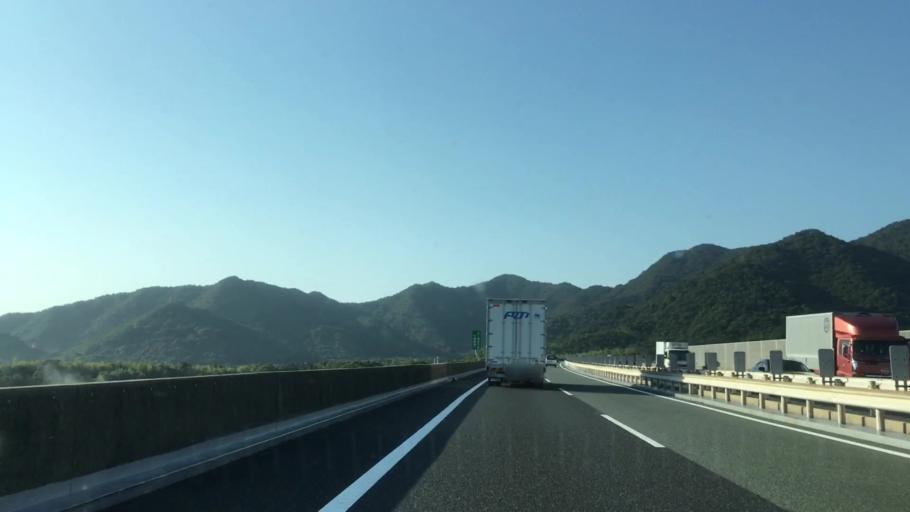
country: JP
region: Yamaguchi
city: Ogori-shimogo
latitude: 34.0931
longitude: 131.4559
